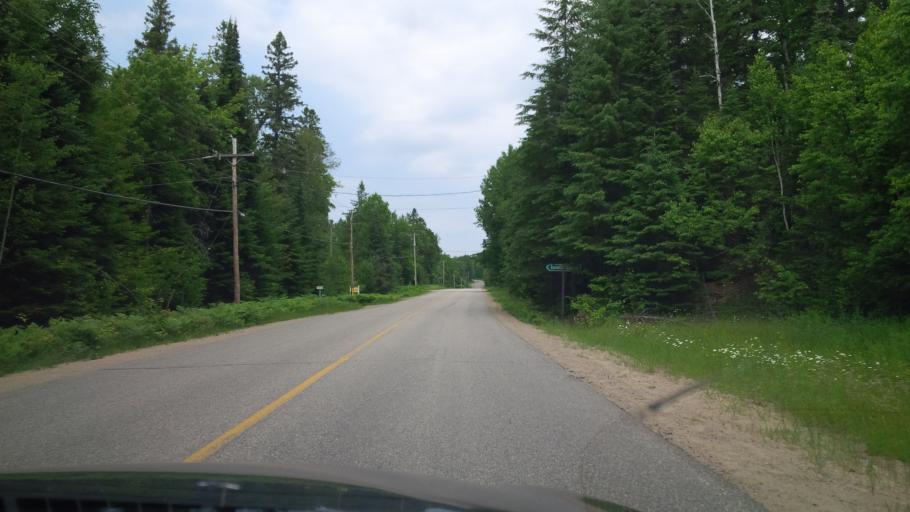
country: CA
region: Ontario
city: Huntsville
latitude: 45.6210
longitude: -79.1556
